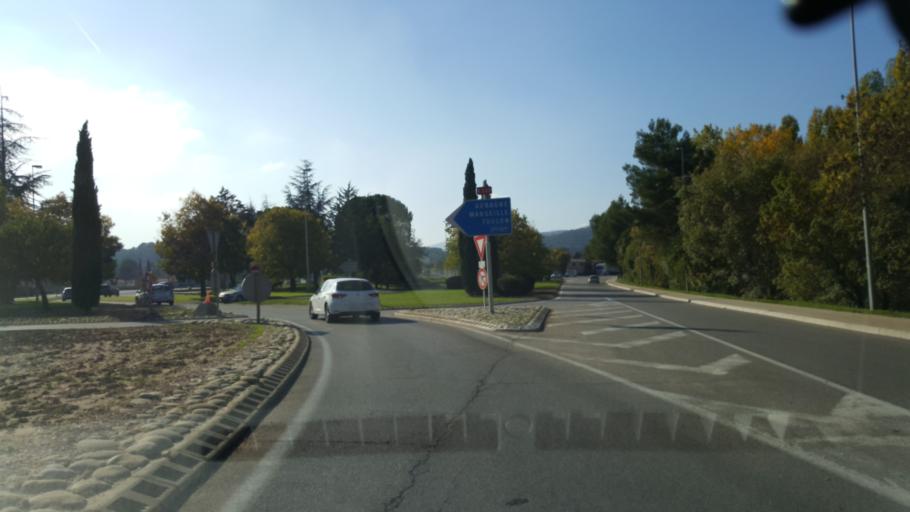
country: FR
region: Provence-Alpes-Cote d'Azur
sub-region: Departement des Bouches-du-Rhone
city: Auriol
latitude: 43.3677
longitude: 5.6459
